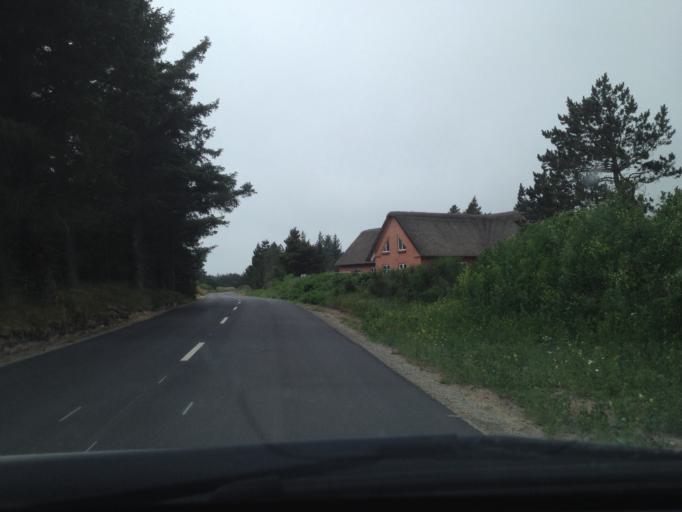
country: DK
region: South Denmark
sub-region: Varde Kommune
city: Oksbol
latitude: 55.5542
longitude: 8.1627
